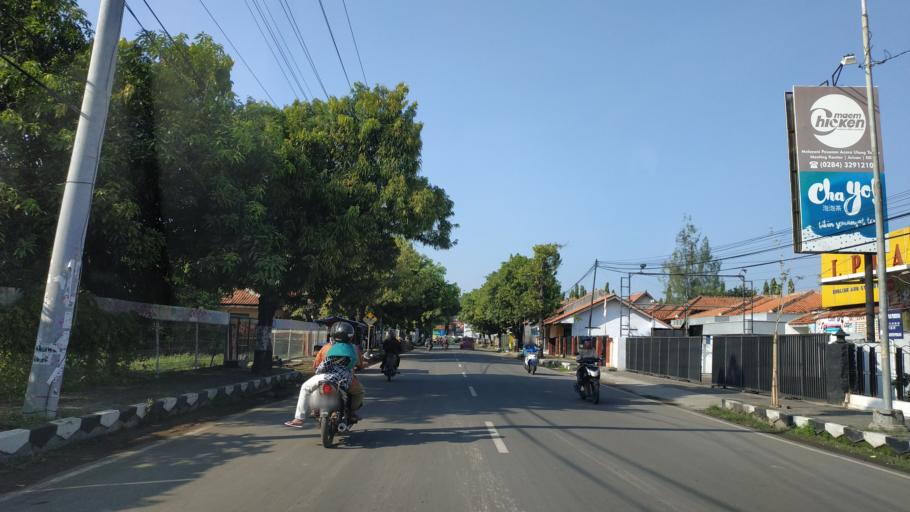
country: ID
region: Central Java
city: Pemalang
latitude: -6.9020
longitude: 109.3878
